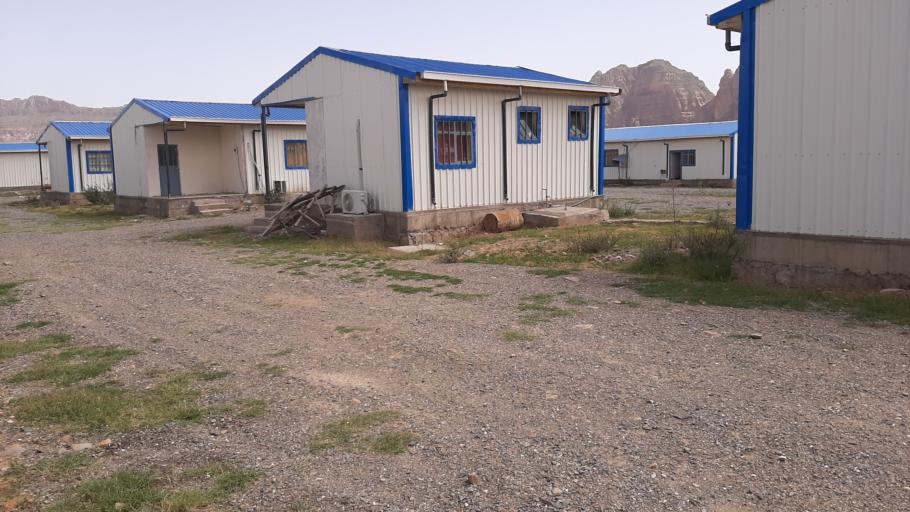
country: ET
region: Tigray
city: Adigrat
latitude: 13.9077
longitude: 39.4046
